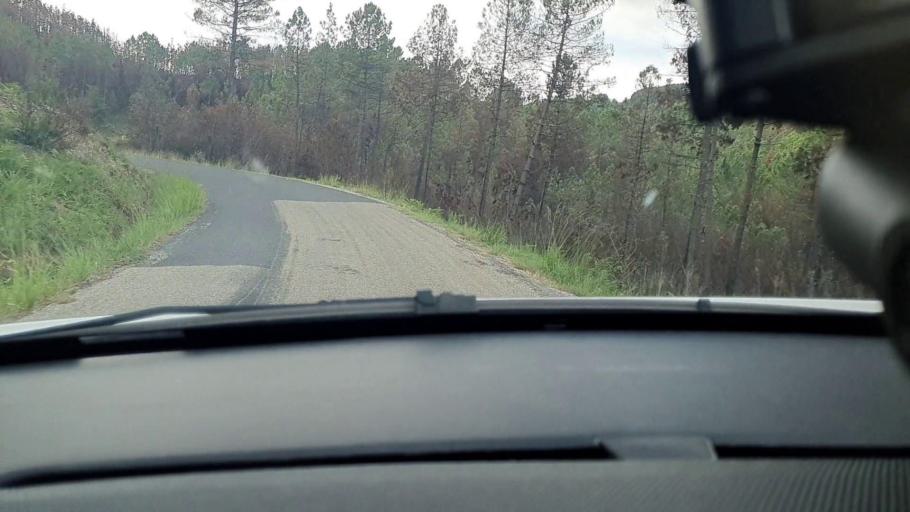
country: FR
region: Languedoc-Roussillon
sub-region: Departement du Gard
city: Besseges
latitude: 44.3270
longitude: 4.0851
